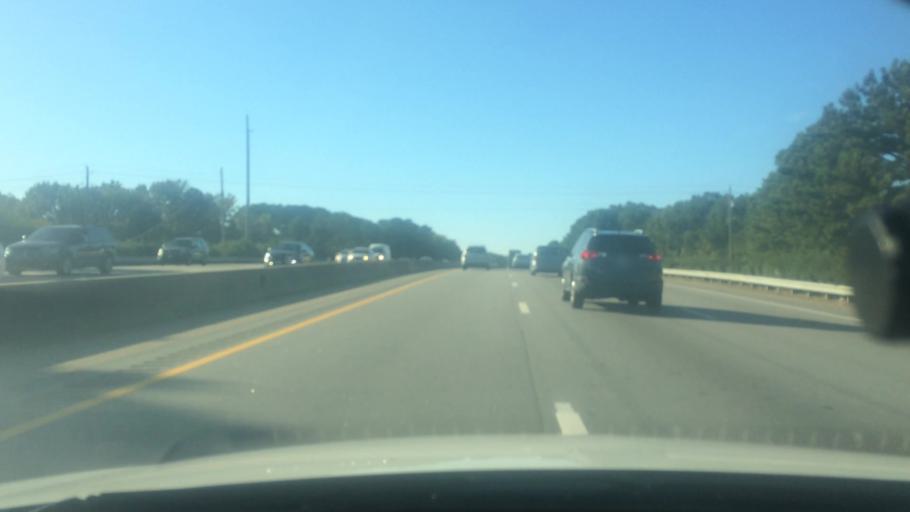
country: US
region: North Carolina
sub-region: Wake County
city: Raleigh
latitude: 35.8250
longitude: -78.6203
